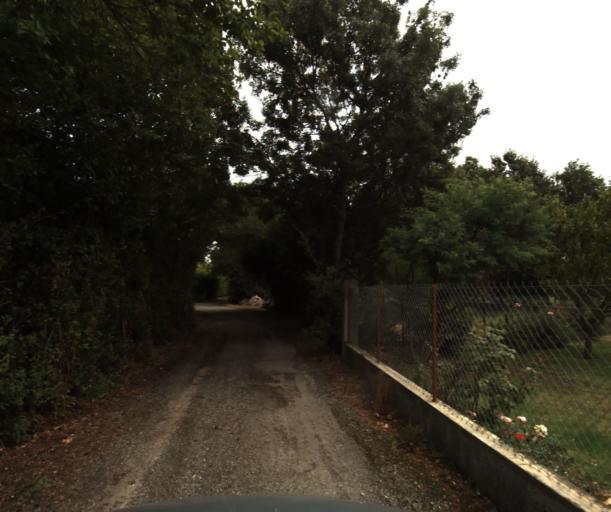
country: FR
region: Midi-Pyrenees
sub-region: Departement de la Haute-Garonne
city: Pinsaguel
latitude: 43.5081
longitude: 1.3870
